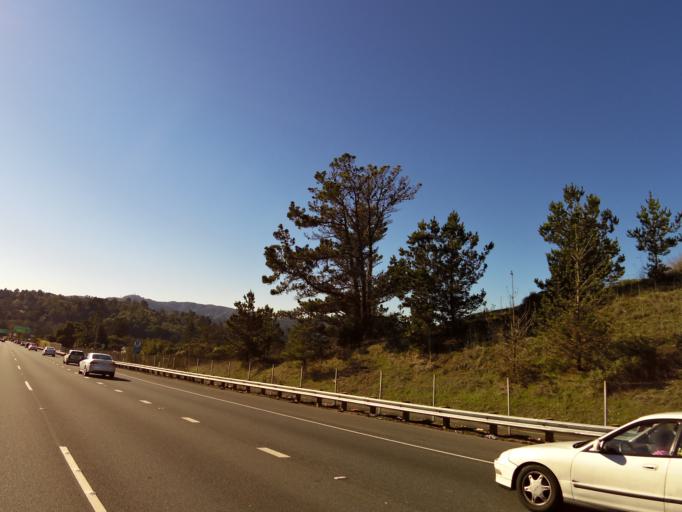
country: US
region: California
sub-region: Marin County
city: Strawberry
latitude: 37.9093
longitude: -122.5139
